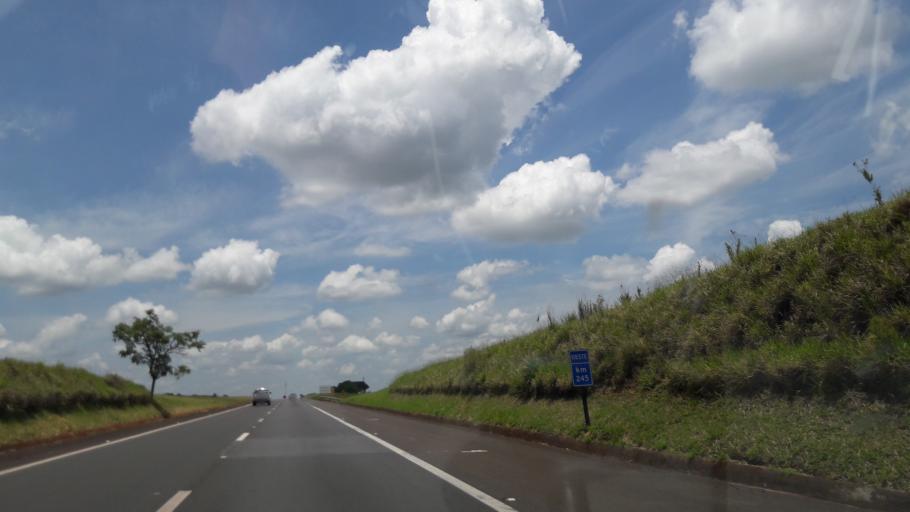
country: BR
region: Sao Paulo
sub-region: Avare
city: Avare
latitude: -22.9557
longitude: -48.8409
